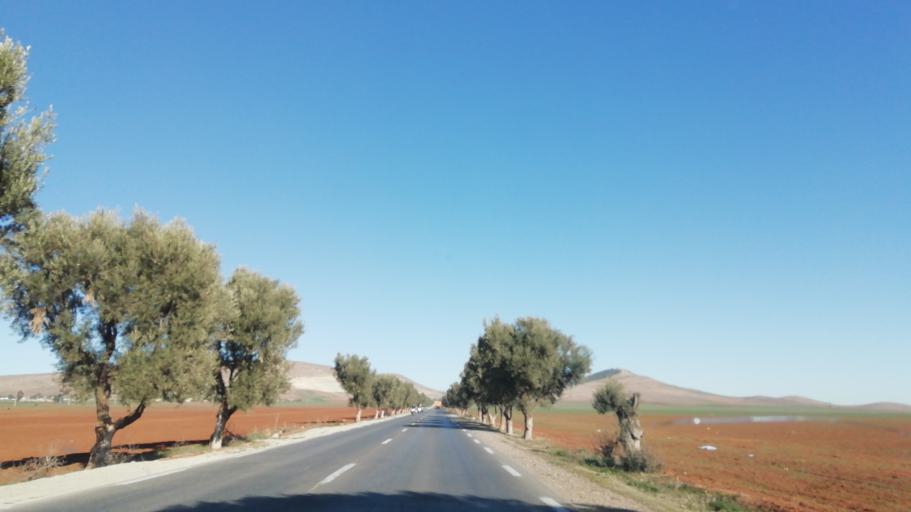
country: DZ
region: Mascara
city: Mascara
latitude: 35.2216
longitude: 0.1134
